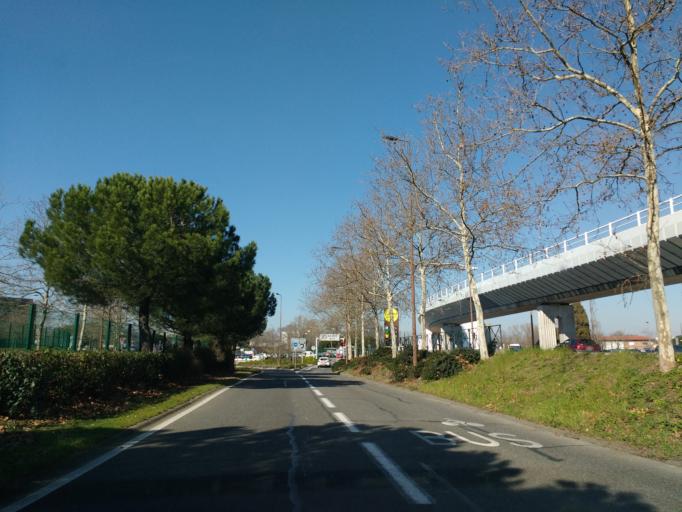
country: FR
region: Midi-Pyrenees
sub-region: Departement de la Haute-Garonne
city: Portet-sur-Garonne
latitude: 43.5683
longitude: 1.3925
